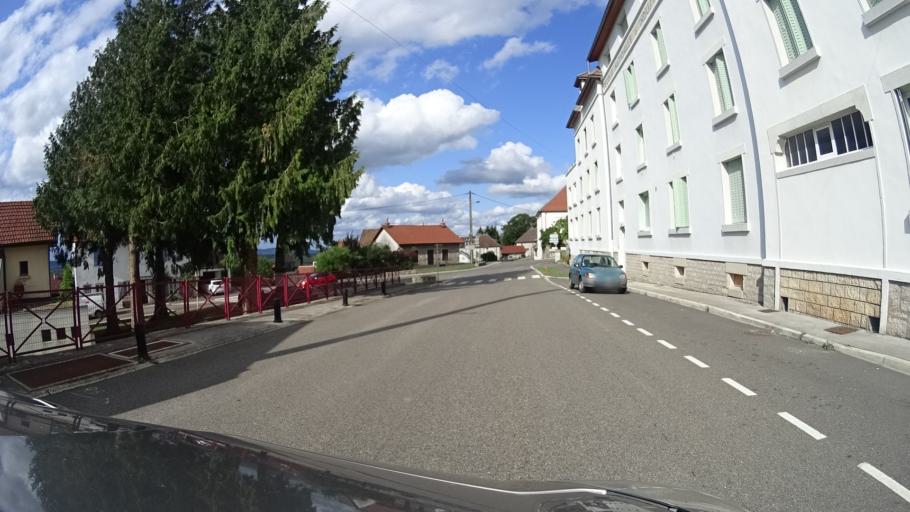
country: FR
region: Franche-Comte
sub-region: Departement du Doubs
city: Mamirolle
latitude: 47.1968
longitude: 6.1618
